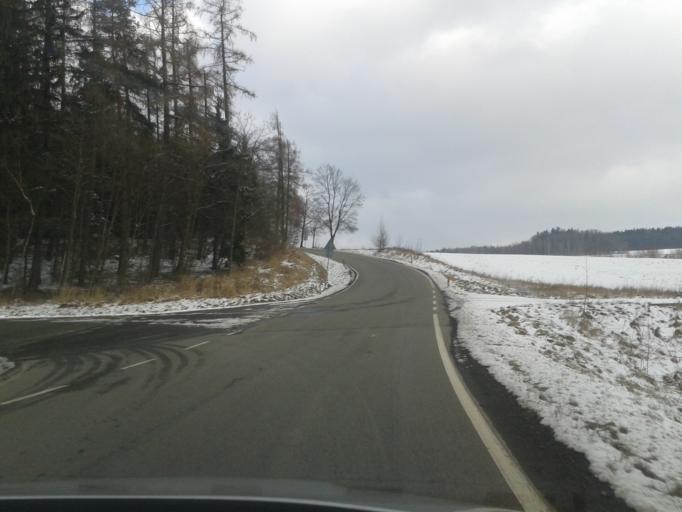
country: CZ
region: Olomoucky
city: Horni Stepanov
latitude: 49.5703
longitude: 16.8200
